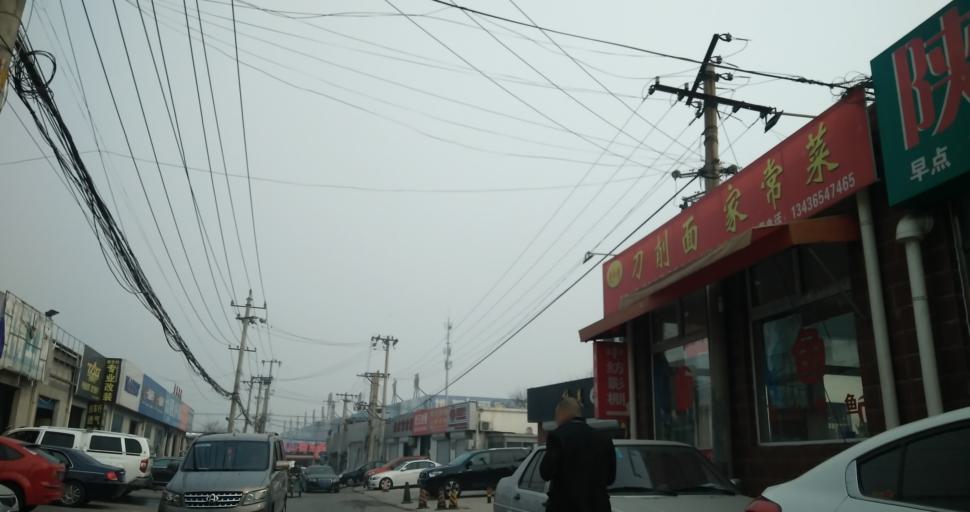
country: CN
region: Beijing
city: Jiugong
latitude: 39.8489
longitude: 116.4803
